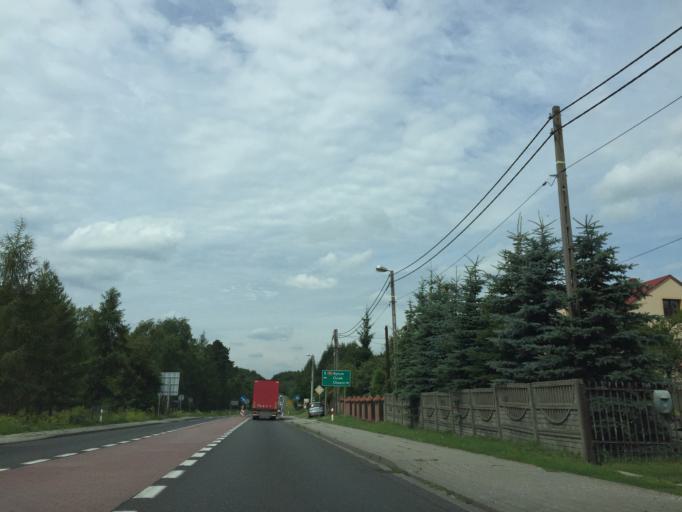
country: PL
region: Lesser Poland Voivodeship
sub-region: Powiat olkuski
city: Osiek
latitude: 50.2680
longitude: 19.6086
